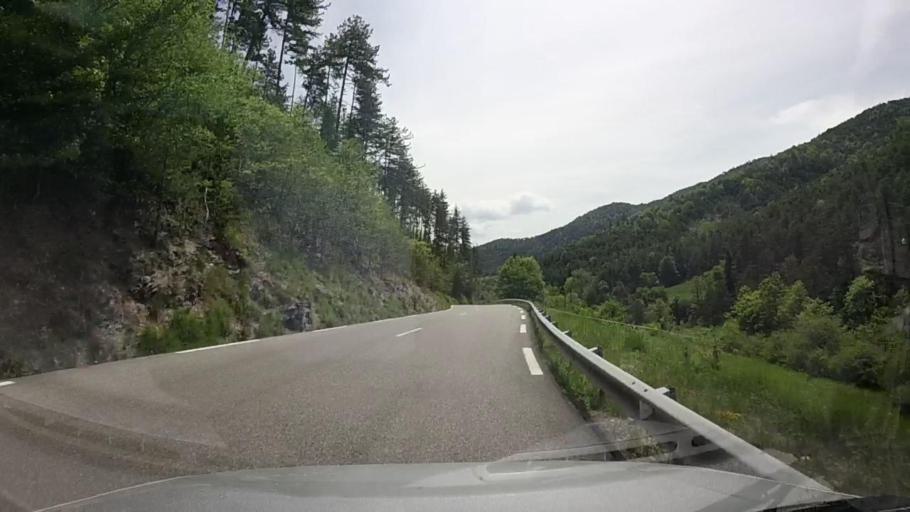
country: FR
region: Provence-Alpes-Cote d'Azur
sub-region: Departement des Alpes-de-Haute-Provence
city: Le Brusquet
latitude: 44.2177
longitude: 6.3614
